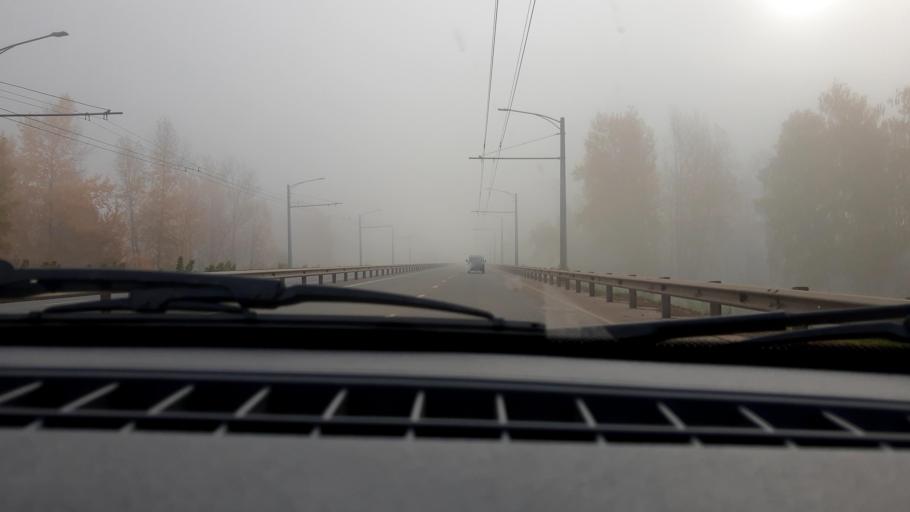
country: RU
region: Bashkortostan
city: Mikhaylovka
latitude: 54.7696
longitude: 55.9163
